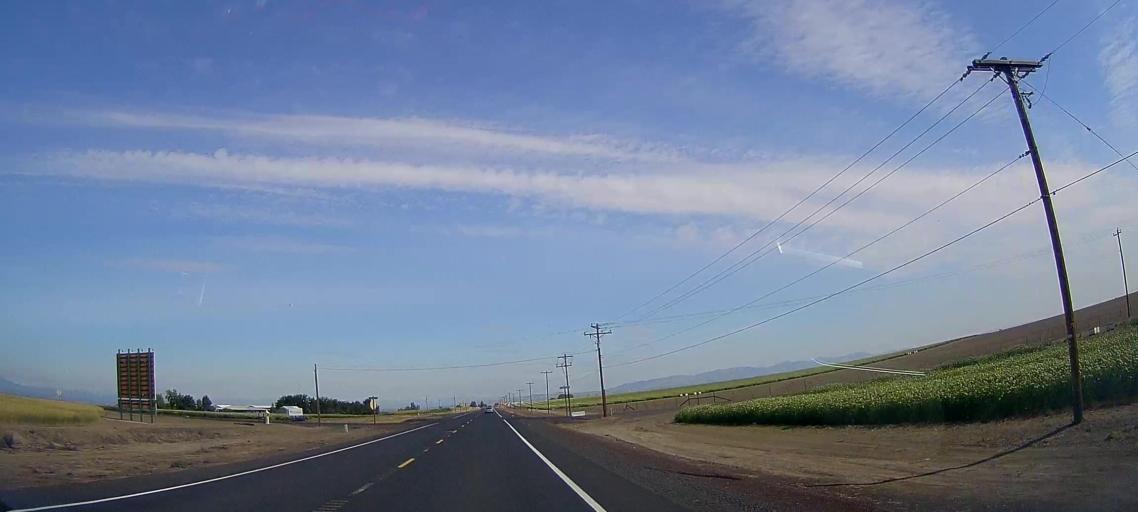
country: US
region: Oregon
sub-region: Jefferson County
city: Madras
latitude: 44.6784
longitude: -121.1460
